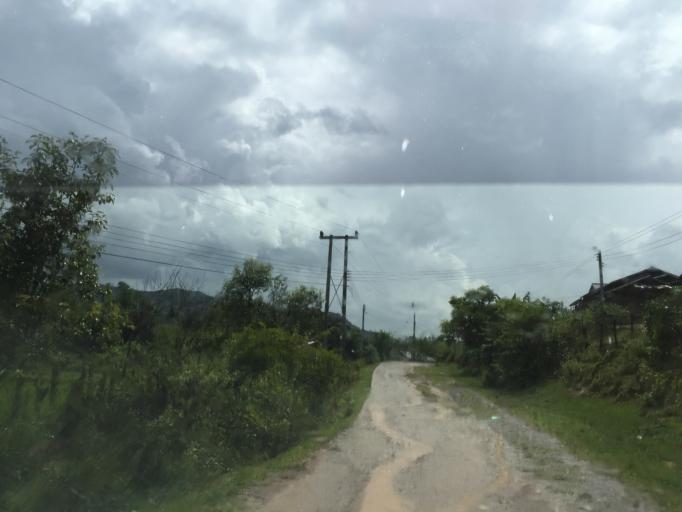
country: LA
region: Xiangkhoang
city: Muang Phonsavan
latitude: 19.3413
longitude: 103.5650
